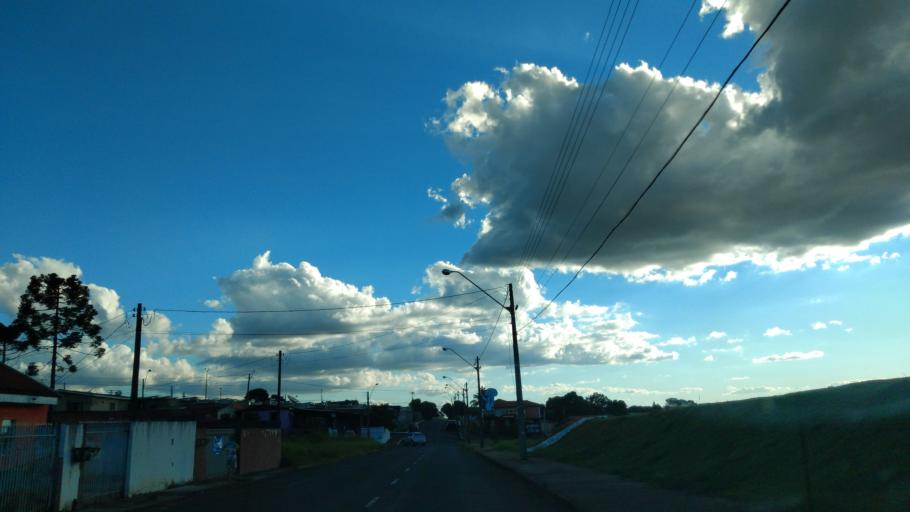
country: BR
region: Parana
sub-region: Guarapuava
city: Guarapuava
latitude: -25.3939
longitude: -51.4797
